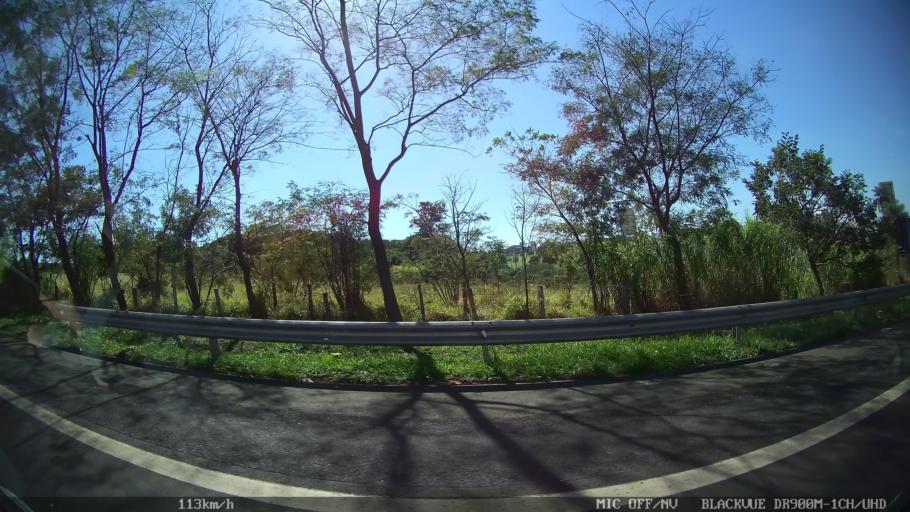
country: BR
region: Sao Paulo
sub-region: Franca
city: Franca
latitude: -20.5549
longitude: -47.4231
